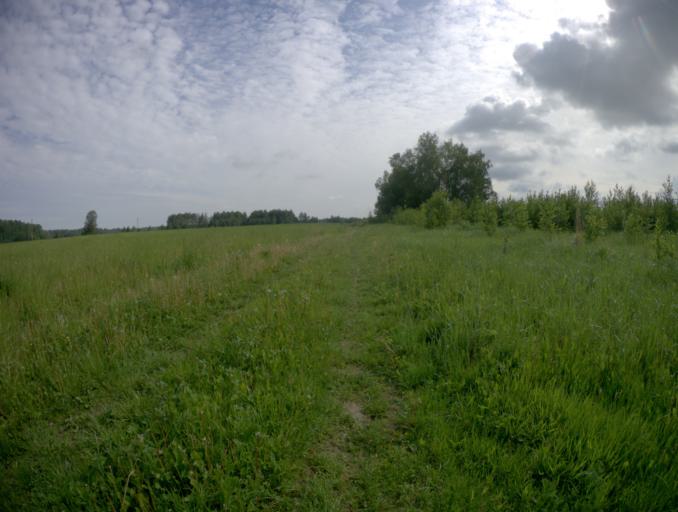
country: RU
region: Vladimir
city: Lakinsk
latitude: 56.0847
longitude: 39.8913
